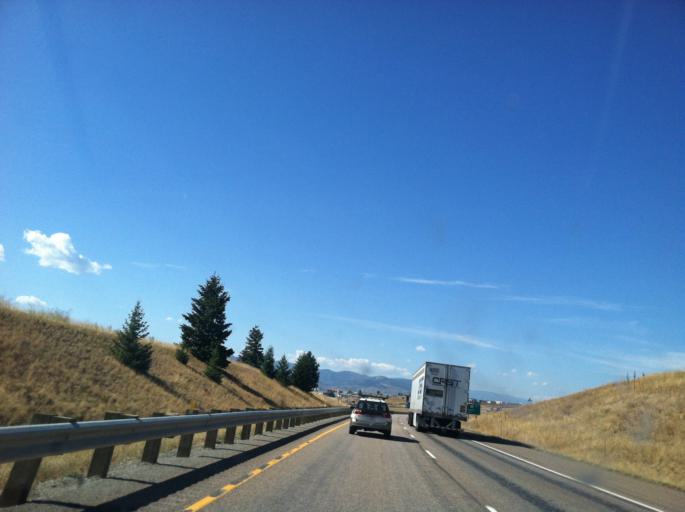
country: US
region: Montana
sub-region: Missoula County
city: Orchard Homes
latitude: 46.9393
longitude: -114.1079
